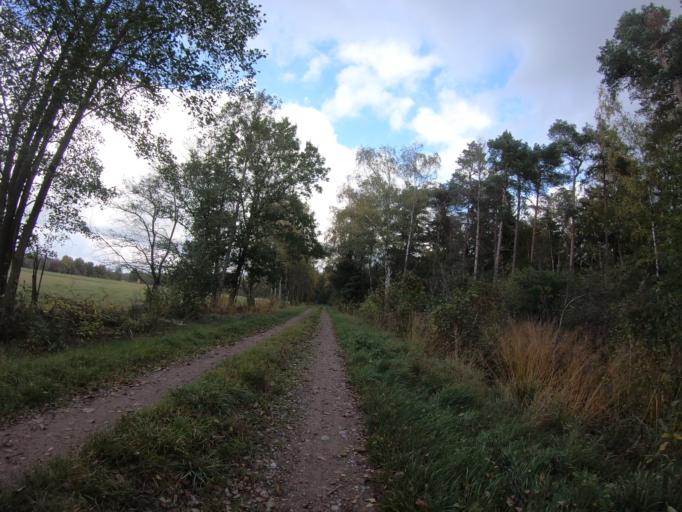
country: DE
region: Lower Saxony
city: Wahrenholz
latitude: 52.5815
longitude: 10.6156
